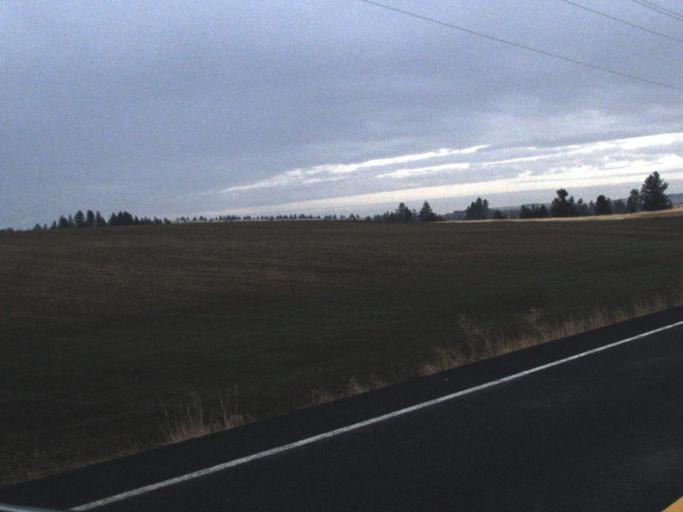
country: US
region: Washington
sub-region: Lincoln County
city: Davenport
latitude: 47.7930
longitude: -118.1737
